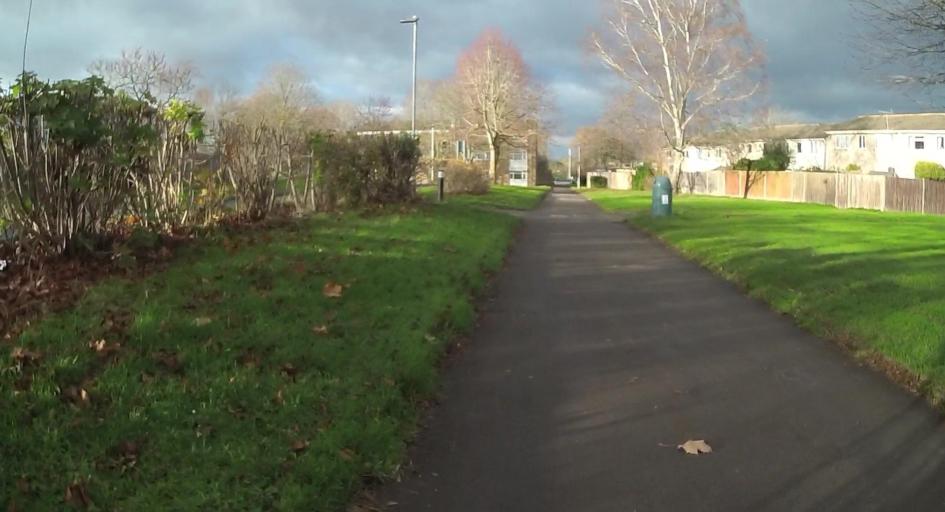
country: GB
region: England
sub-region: Bracknell Forest
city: Bracknell
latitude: 51.4019
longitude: -0.7712
